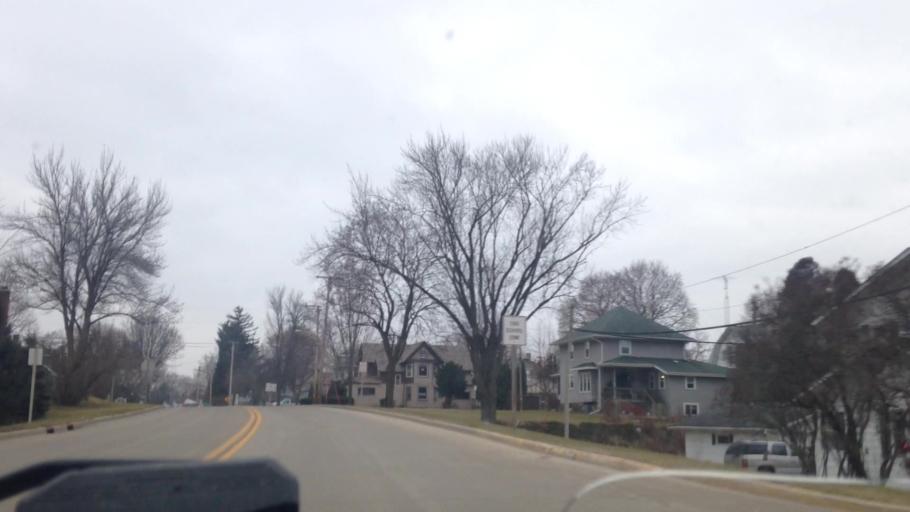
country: US
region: Wisconsin
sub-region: Dodge County
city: Horicon
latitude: 43.4543
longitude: -88.6231
